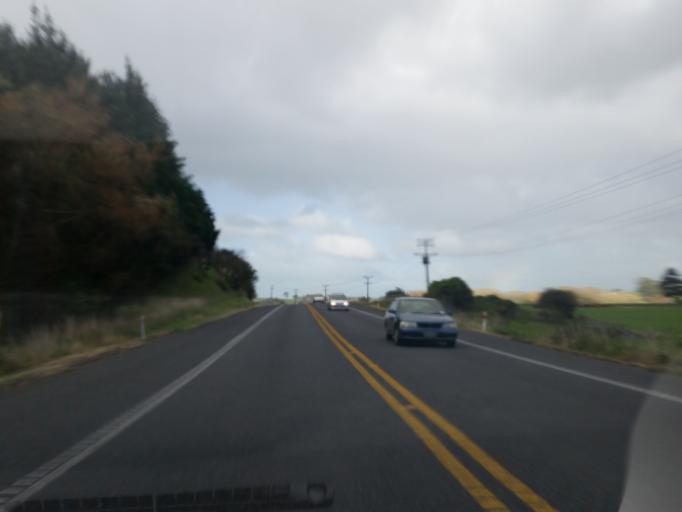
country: NZ
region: Auckland
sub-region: Auckland
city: Pukekohe East
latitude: -37.2150
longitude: 175.0873
